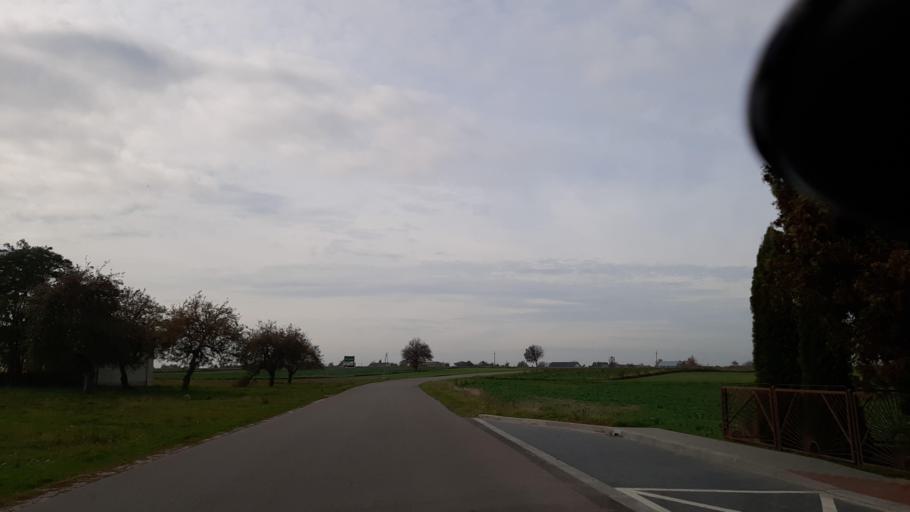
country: PL
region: Lublin Voivodeship
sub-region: Powiat lubelski
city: Garbow
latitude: 51.3847
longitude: 22.3739
